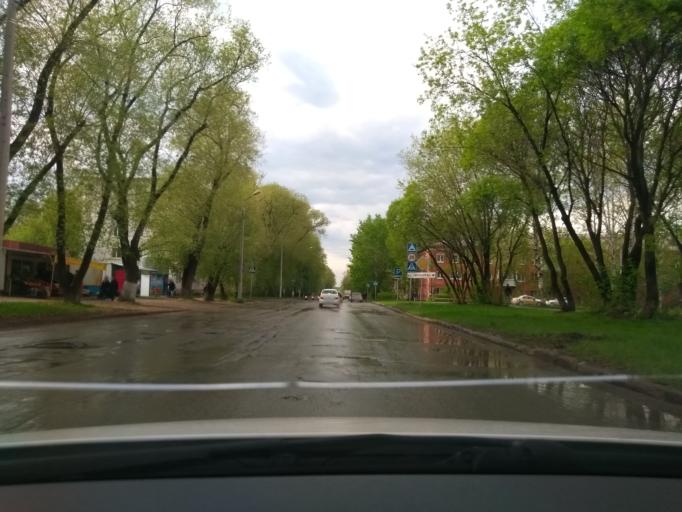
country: RU
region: Perm
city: Perm
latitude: 57.9978
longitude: 56.3024
